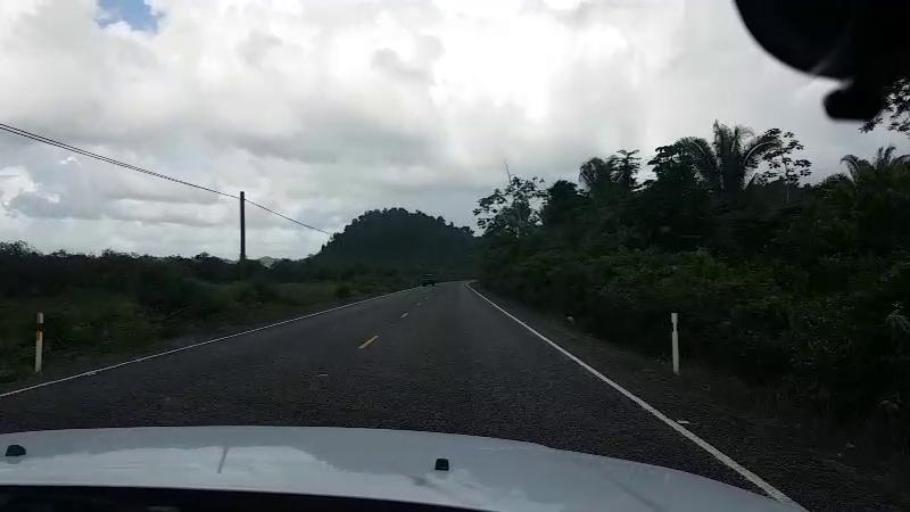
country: BZ
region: Cayo
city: Belmopan
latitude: 17.1530
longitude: -88.6927
